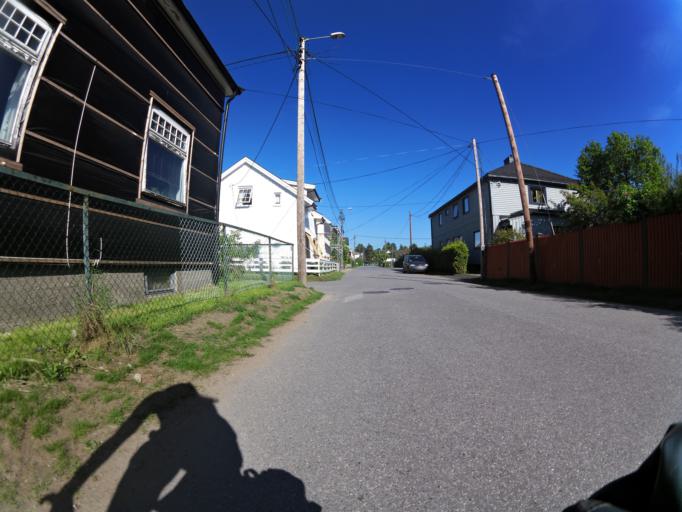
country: NO
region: Ostfold
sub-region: Fredrikstad
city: Fredrikstad
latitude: 59.2293
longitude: 10.9960
